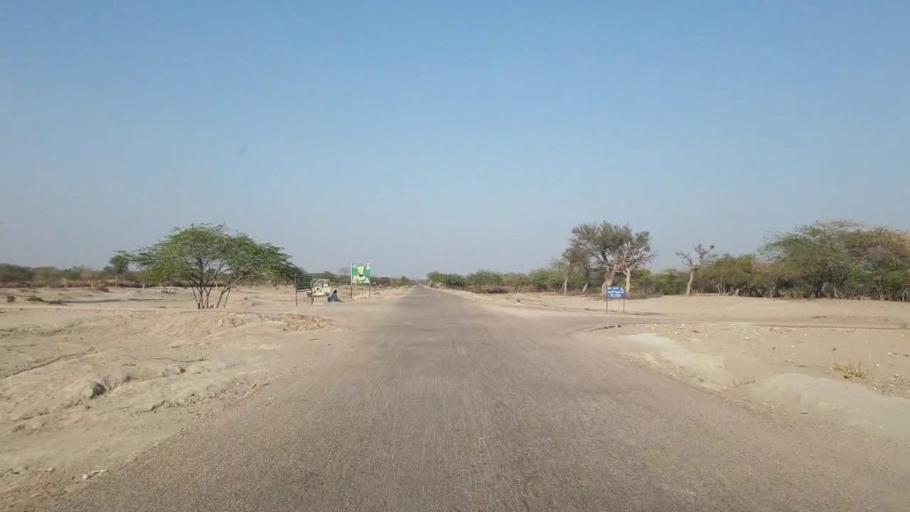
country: PK
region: Sindh
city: Chor
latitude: 25.5567
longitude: 69.7935
